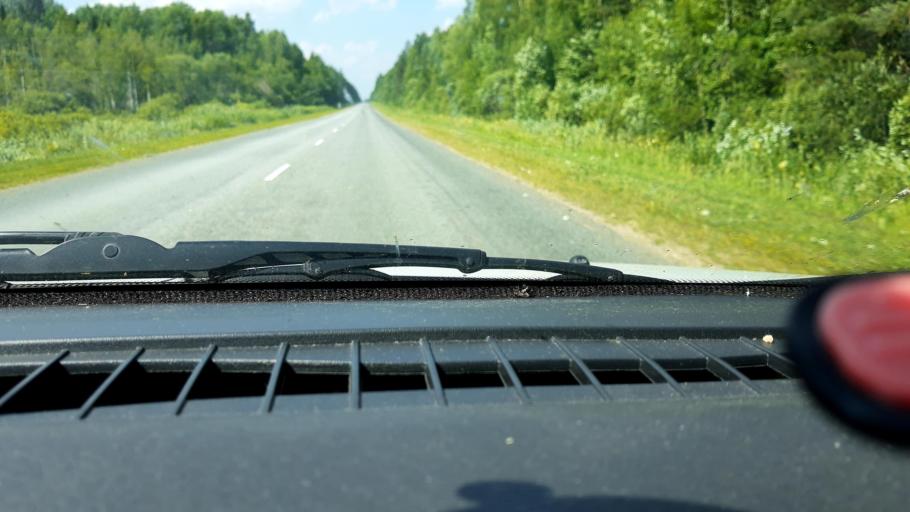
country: RU
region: Nizjnij Novgorod
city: Sharanga
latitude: 57.2274
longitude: 46.4963
